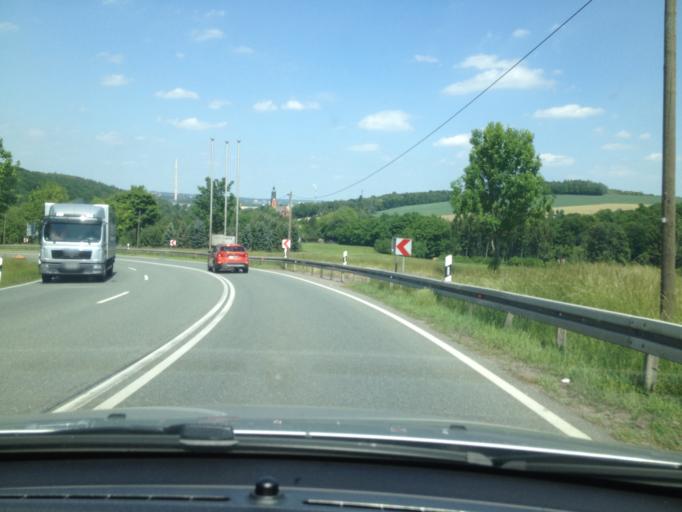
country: DE
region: Saxony
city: Burkhardtsdorf
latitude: 50.7710
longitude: 12.9281
